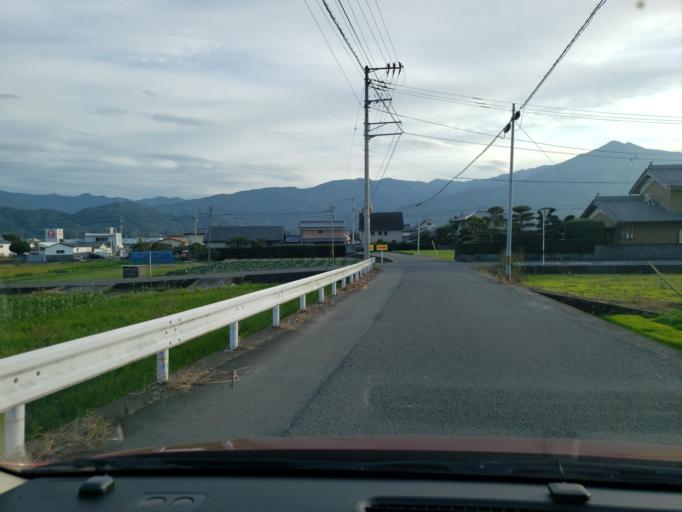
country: JP
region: Tokushima
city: Wakimachi
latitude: 34.0760
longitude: 134.2278
